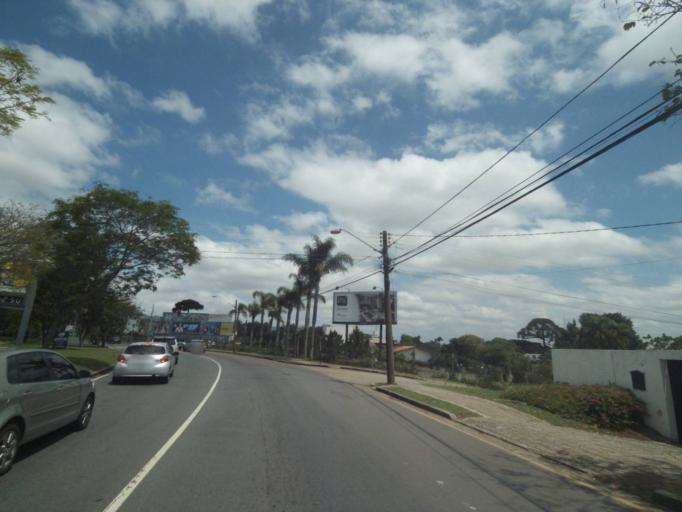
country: BR
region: Parana
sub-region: Curitiba
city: Curitiba
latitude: -25.4164
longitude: -49.2419
